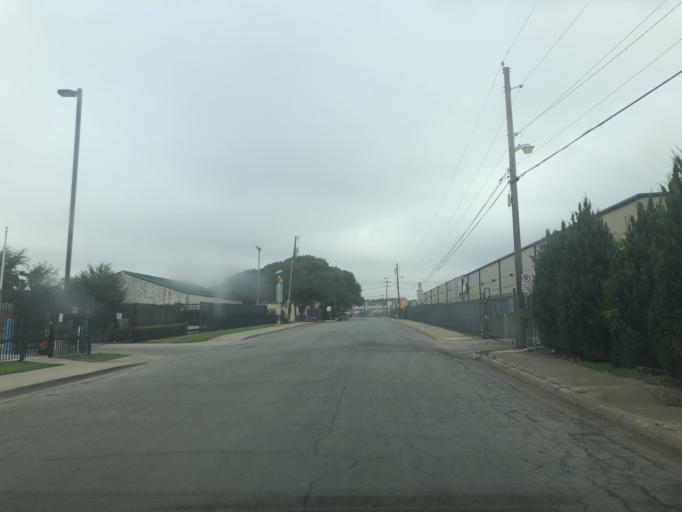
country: US
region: Texas
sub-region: Dallas County
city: University Park
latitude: 32.8602
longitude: -96.8632
